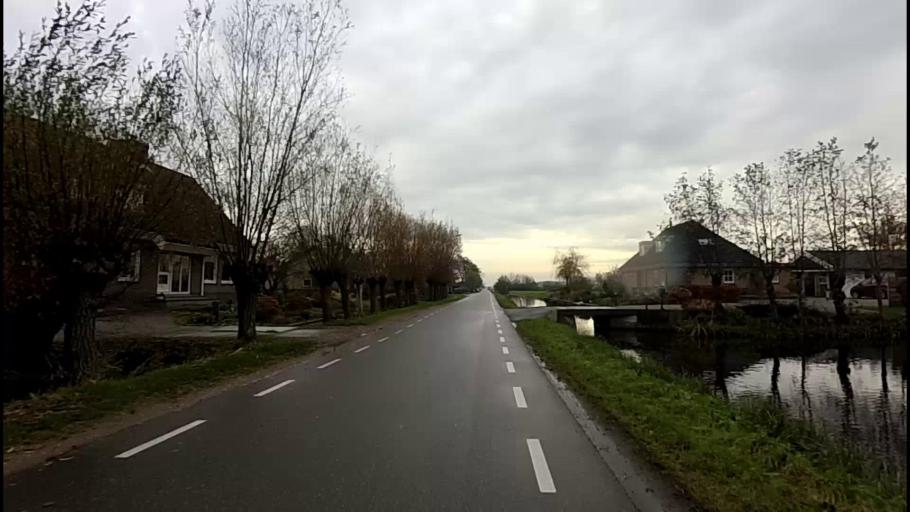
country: NL
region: South Holland
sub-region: Gemeente Krimpen aan den IJssel
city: Krimpen aan den IJssel
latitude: 51.9253
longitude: 4.6483
